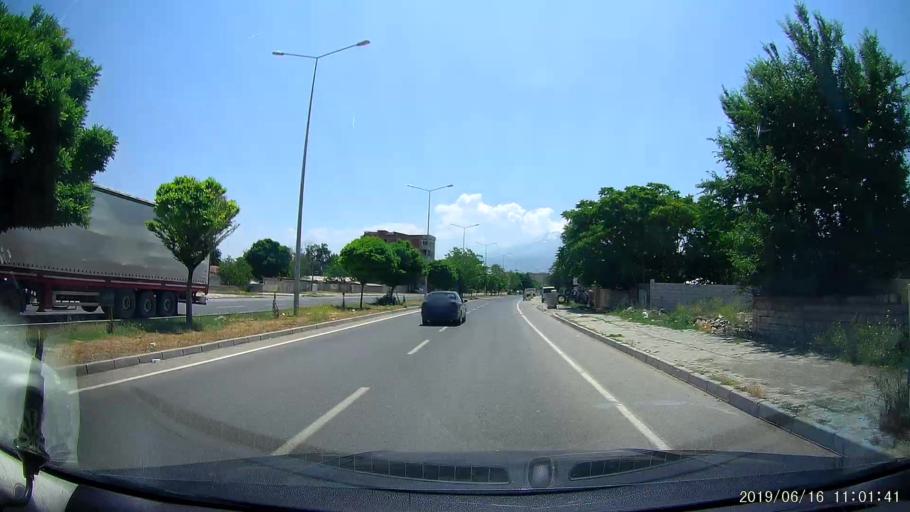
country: TR
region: Igdir
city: Igdir
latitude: 39.9134
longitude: 44.0523
